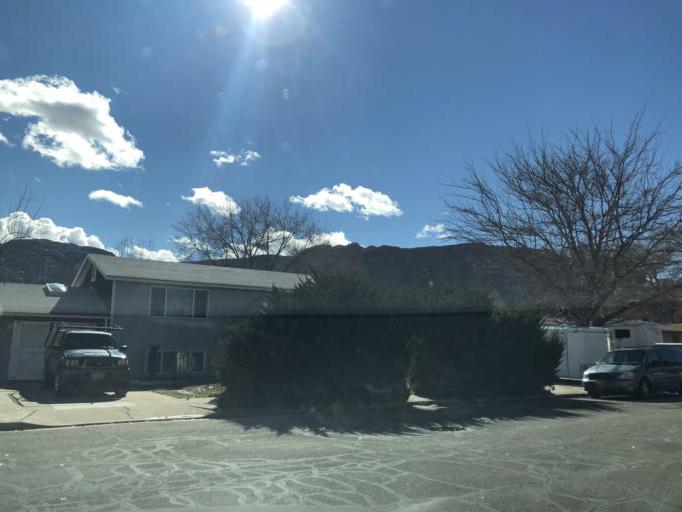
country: US
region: Utah
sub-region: Grand County
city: Moab
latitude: 38.5773
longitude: -109.5600
